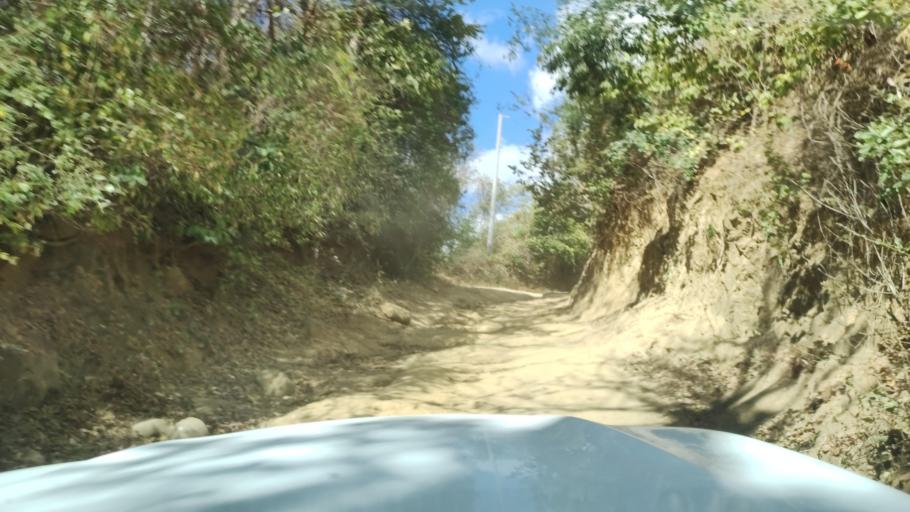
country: NI
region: Carazo
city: Santa Teresa
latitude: 11.6551
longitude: -86.1859
